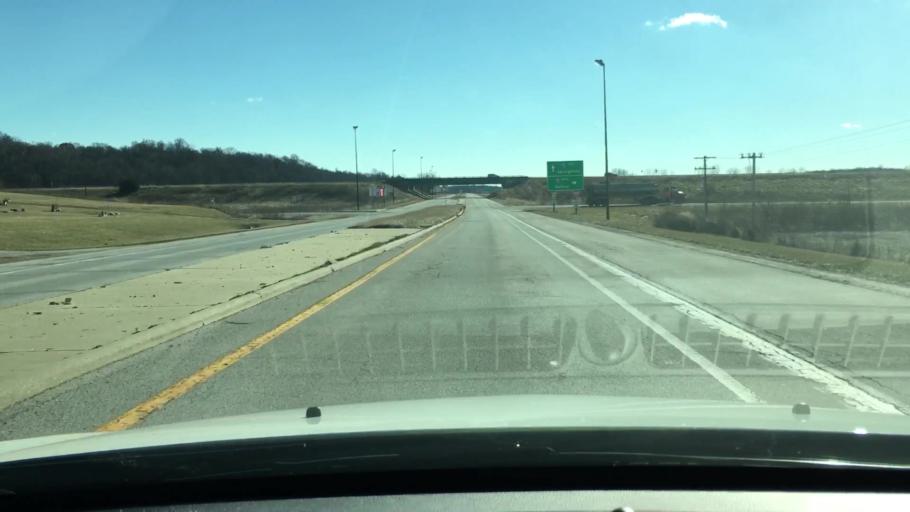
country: US
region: Illinois
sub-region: Scott County
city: Winchester
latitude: 39.6884
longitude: -90.5709
